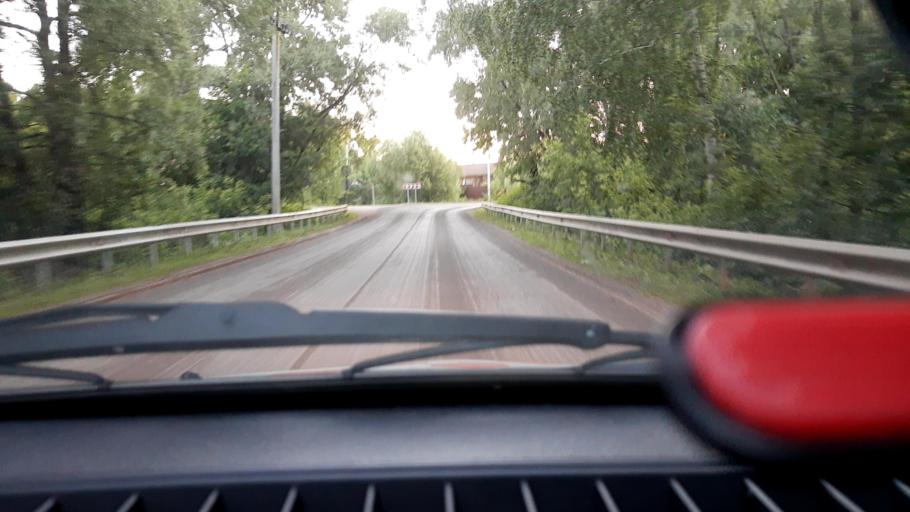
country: RU
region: Bashkortostan
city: Avdon
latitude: 54.6380
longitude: 55.6991
